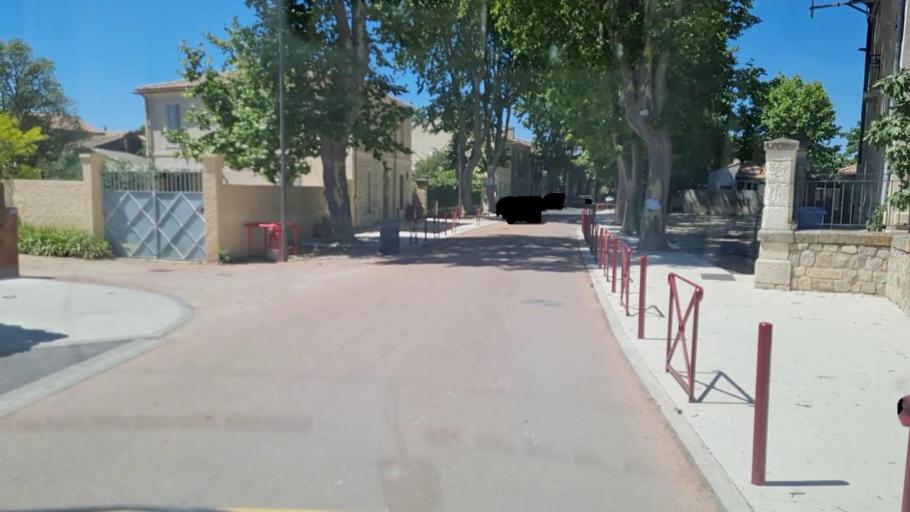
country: FR
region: Languedoc-Roussillon
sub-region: Departement du Gard
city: Le Cailar
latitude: 43.6772
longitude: 4.2363
